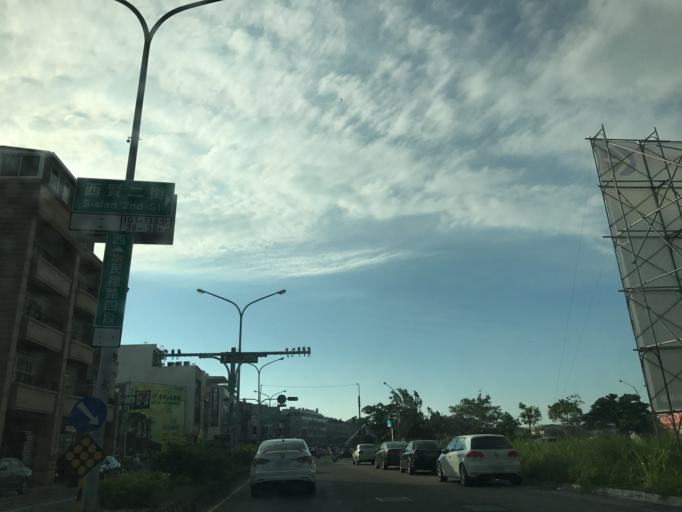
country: TW
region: Taiwan
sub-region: Tainan
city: Tainan
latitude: 22.9993
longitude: 120.1767
